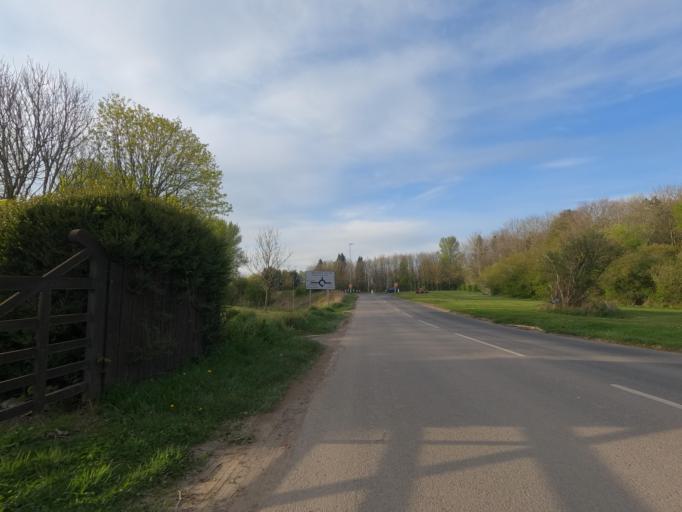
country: GB
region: England
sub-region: Northumberland
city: Cramlington
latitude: 55.0866
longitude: -1.6135
